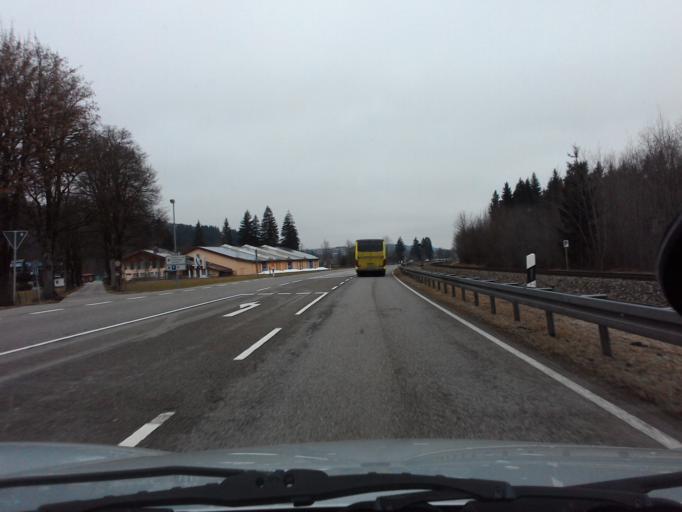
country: DE
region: Bavaria
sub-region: Swabia
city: Oberstdorf
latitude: 47.4466
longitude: 10.2732
